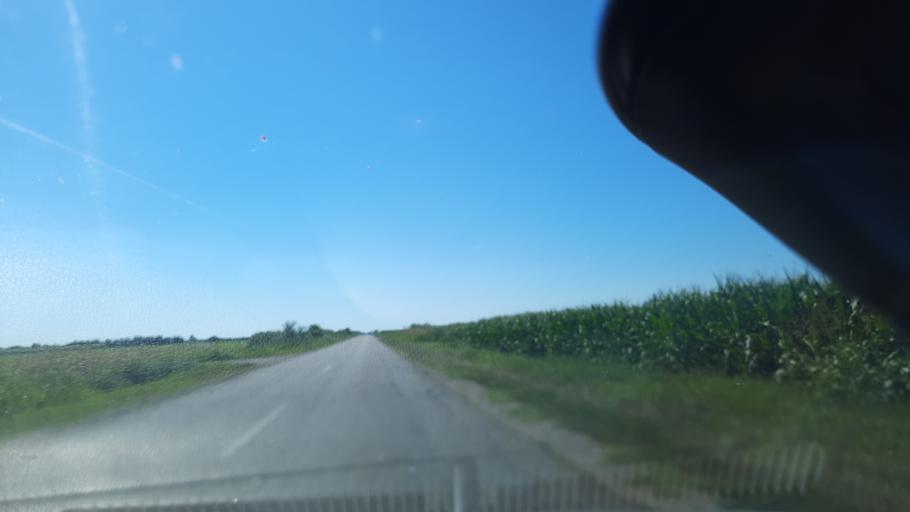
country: RS
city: Simanovci
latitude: 44.8801
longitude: 20.0515
